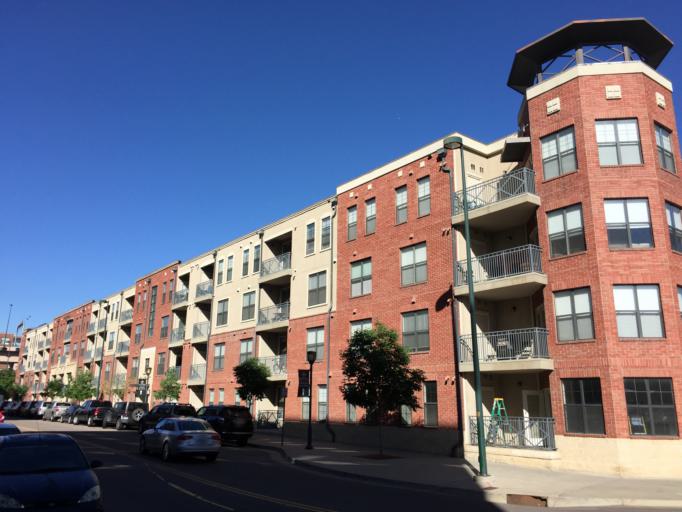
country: US
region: Colorado
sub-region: Denver County
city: Denver
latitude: 39.7583
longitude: -104.9961
